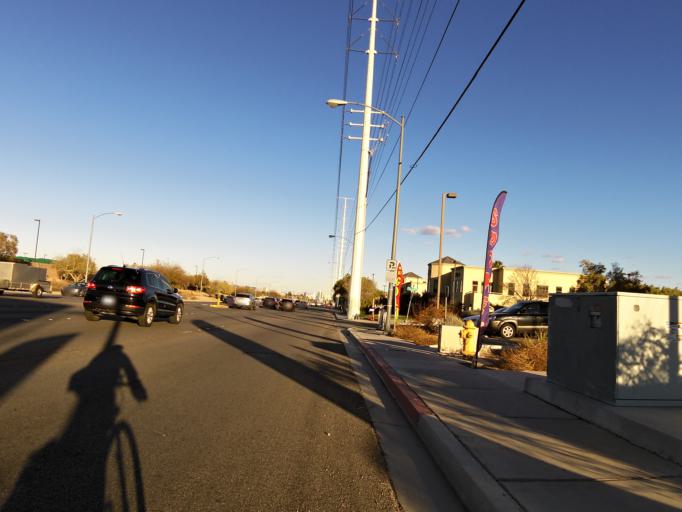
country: US
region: Nevada
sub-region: Clark County
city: Spring Valley
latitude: 36.1147
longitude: -115.2751
